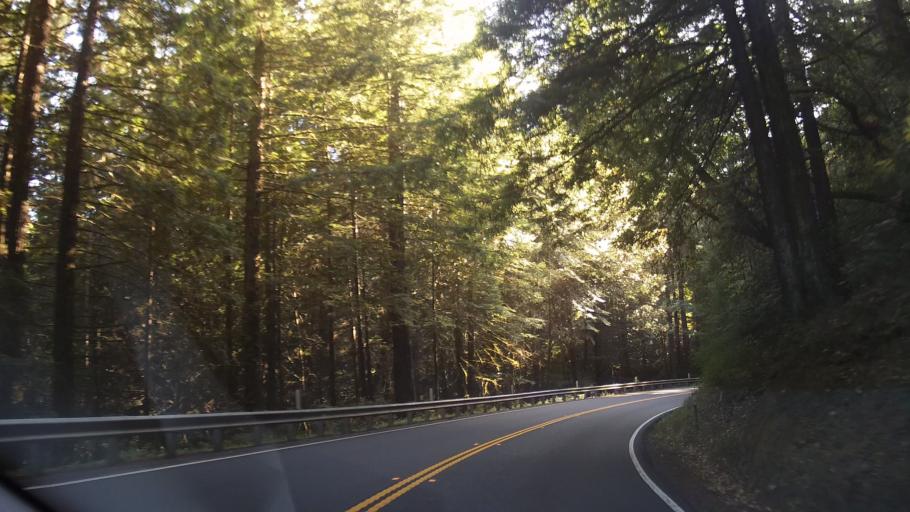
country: US
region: California
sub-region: Mendocino County
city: Brooktrails
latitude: 39.3464
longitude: -123.5947
